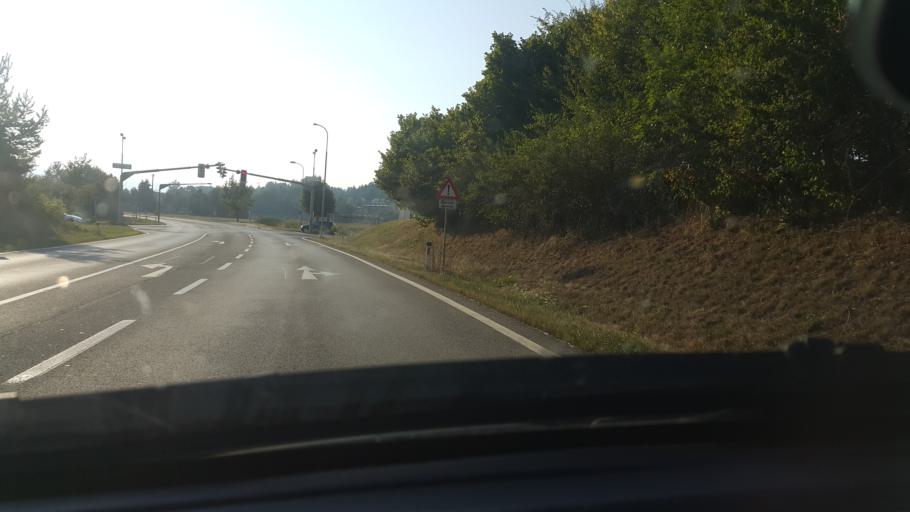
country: AT
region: Carinthia
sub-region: Klagenfurt am Woerthersee
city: Klagenfurt am Woerthersee
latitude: 46.6649
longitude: 14.2768
